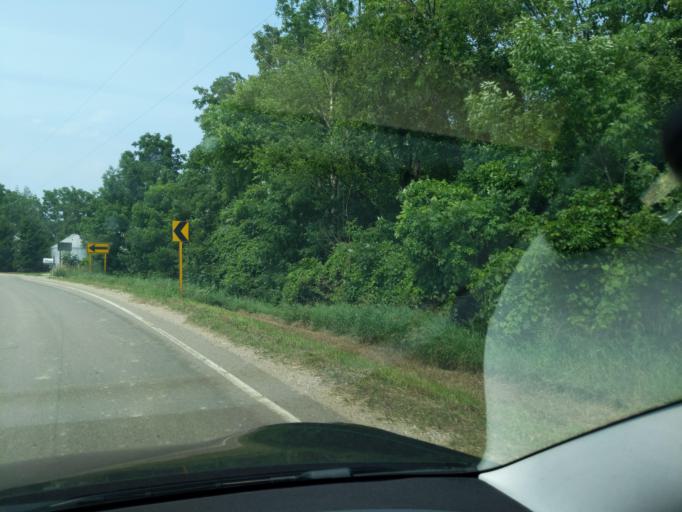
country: US
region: Michigan
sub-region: Clinton County
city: DeWitt
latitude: 42.8942
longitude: -84.5724
